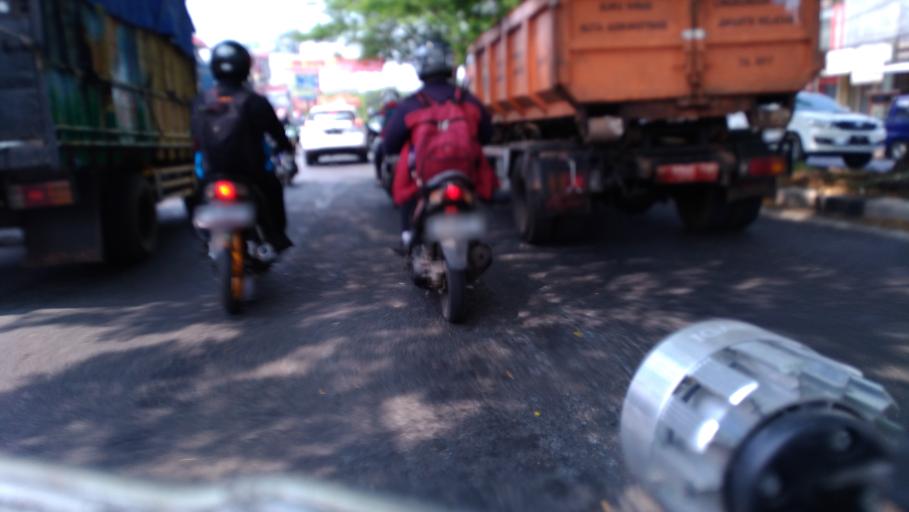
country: ID
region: West Java
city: Cileungsir
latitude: -6.3865
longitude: 106.9385
